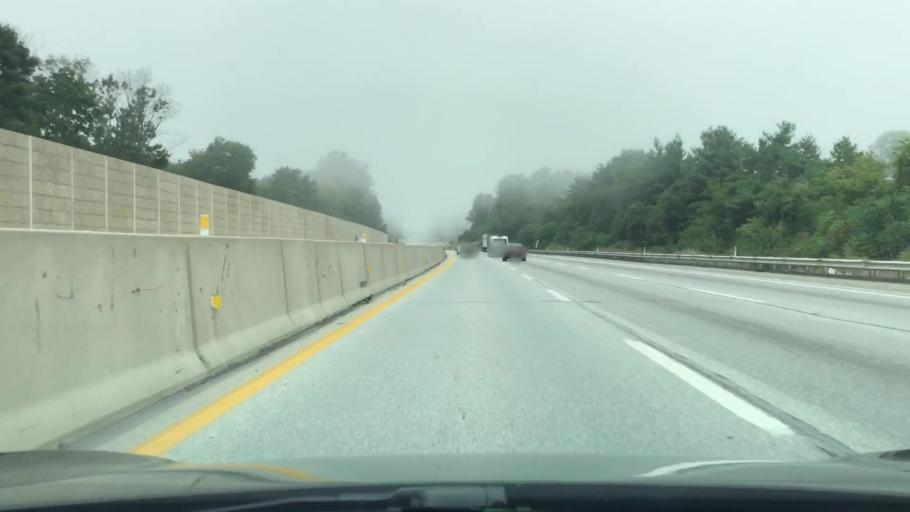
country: US
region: Pennsylvania
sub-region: Bucks County
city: Feasterville
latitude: 40.1445
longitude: -75.0062
